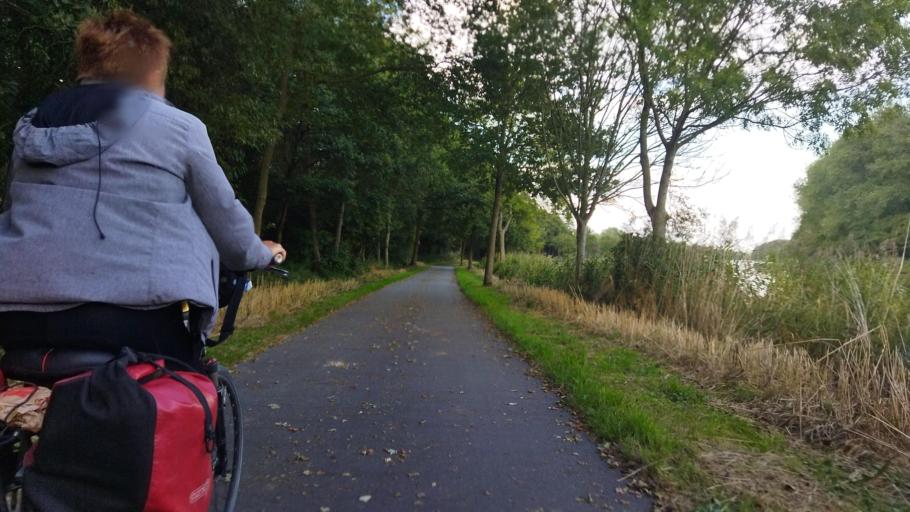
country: DE
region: Lower Saxony
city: Dersum
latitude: 52.9549
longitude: 7.2930
